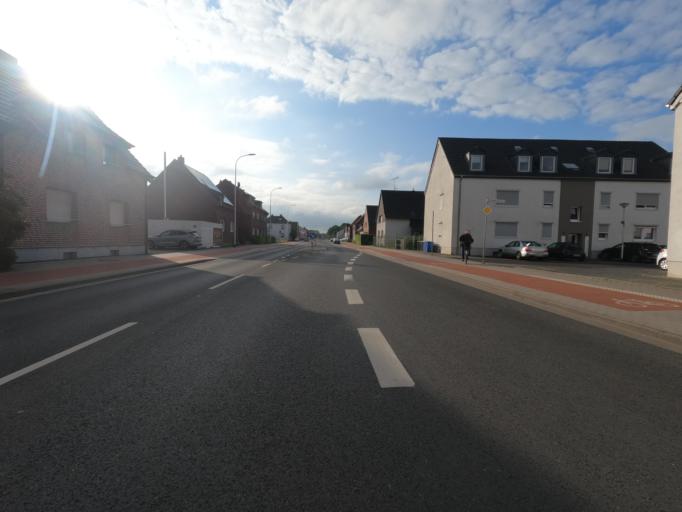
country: DE
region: North Rhine-Westphalia
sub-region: Regierungsbezirk Koln
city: Heinsberg
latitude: 51.0588
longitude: 6.1234
